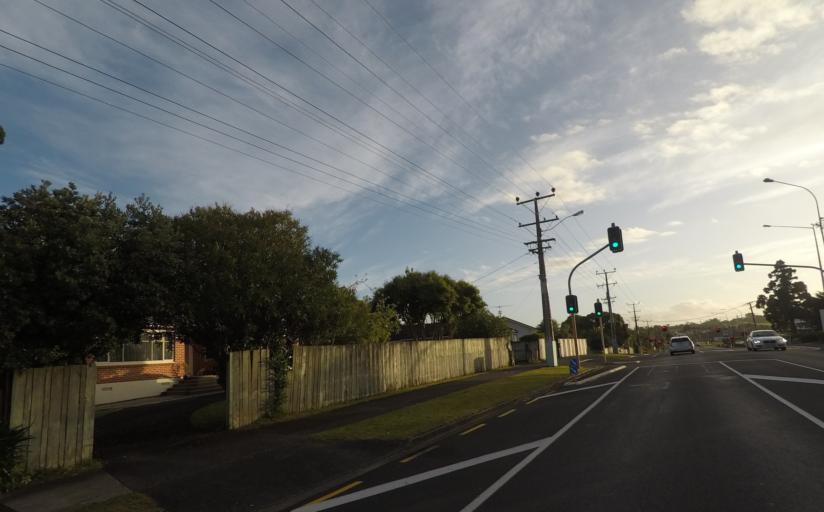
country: NZ
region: Auckland
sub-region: Auckland
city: Rosebank
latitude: -36.8052
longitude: 174.6377
